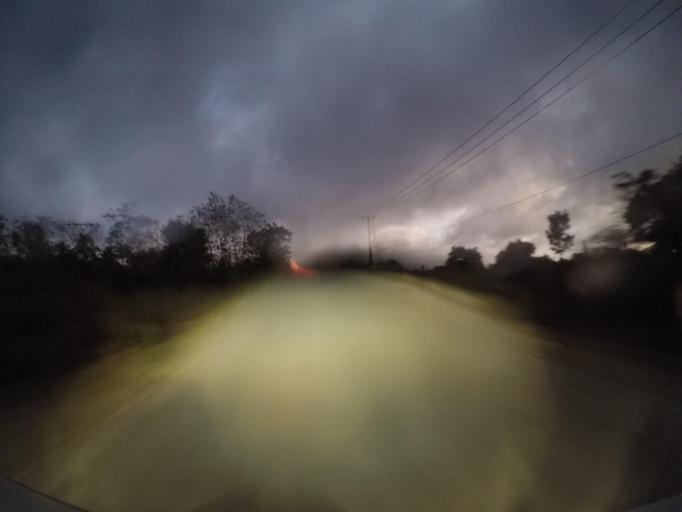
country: TL
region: Lautem
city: Lospalos
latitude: -8.4322
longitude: 127.0039
